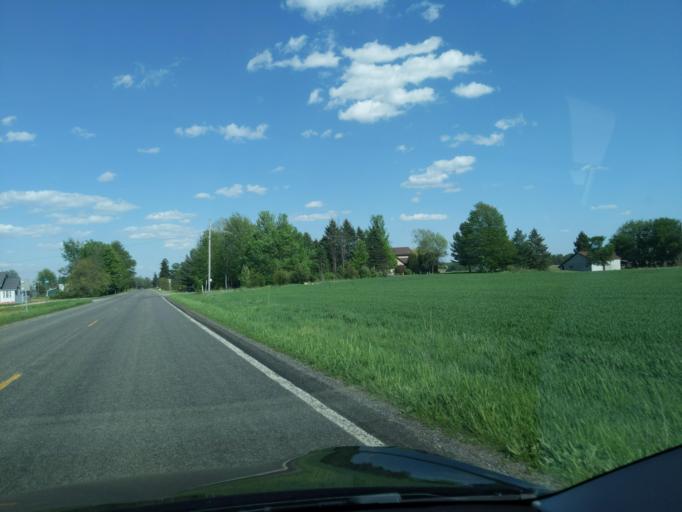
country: US
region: Michigan
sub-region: Ionia County
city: Lake Odessa
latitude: 42.7844
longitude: -85.1741
